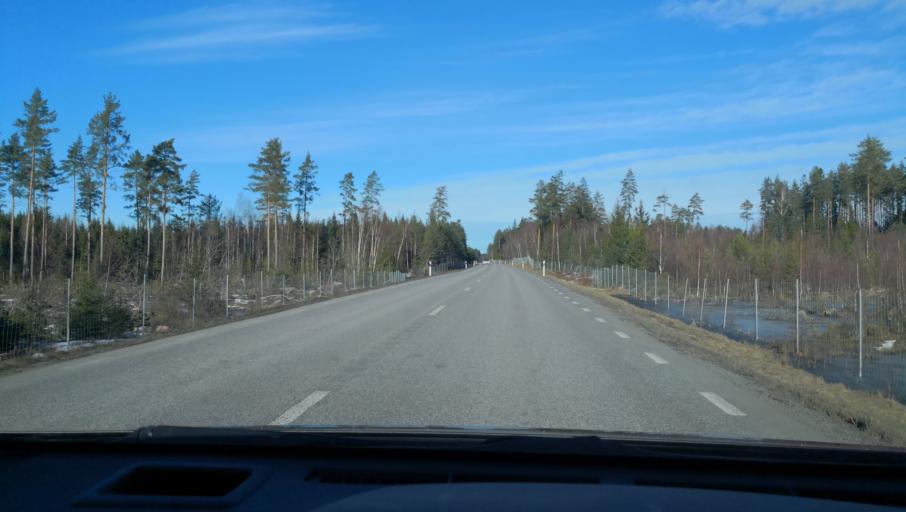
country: SE
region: Uppsala
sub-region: Uppsala Kommun
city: Vattholma
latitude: 60.0423
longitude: 17.7511
